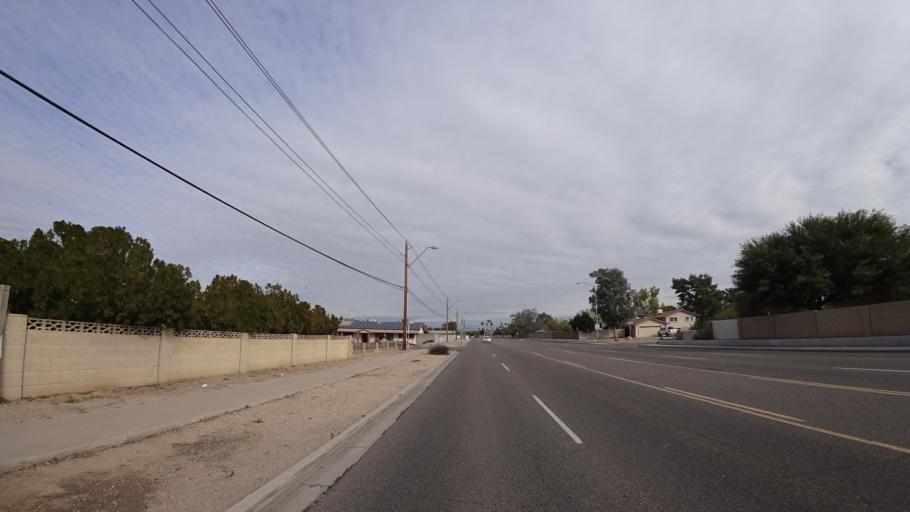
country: US
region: Arizona
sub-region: Maricopa County
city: Glendale
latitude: 33.6302
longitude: -112.1512
